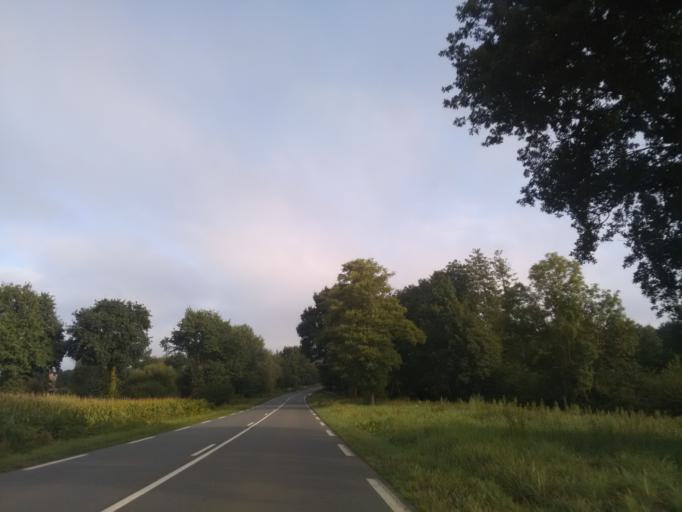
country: FR
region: Brittany
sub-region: Departement d'Ille-et-Vilaine
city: Geveze
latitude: 48.2330
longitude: -1.8040
